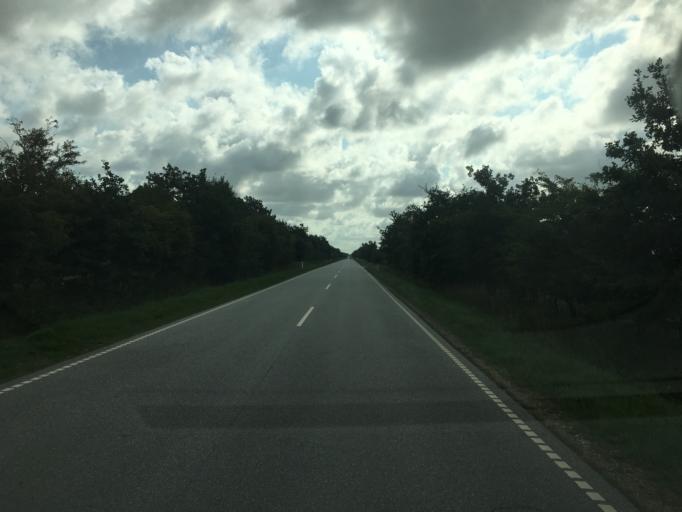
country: DK
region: South Denmark
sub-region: Tonder Kommune
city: Sherrebek
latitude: 55.1254
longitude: 8.8140
